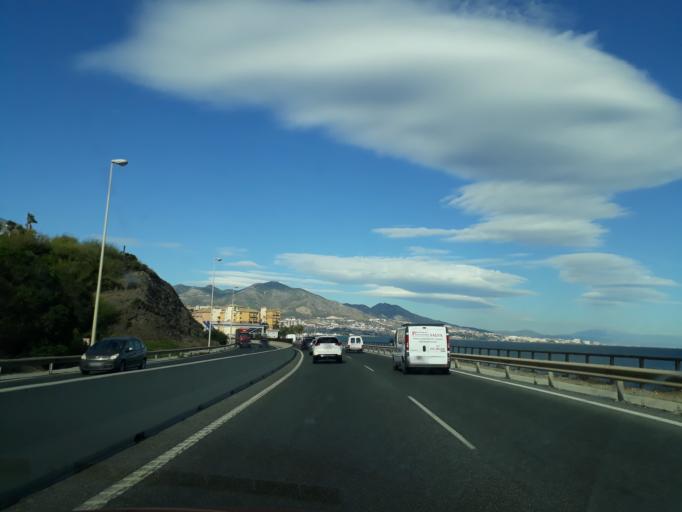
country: ES
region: Andalusia
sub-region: Provincia de Malaga
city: Fuengirola
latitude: 36.5175
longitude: -4.6308
